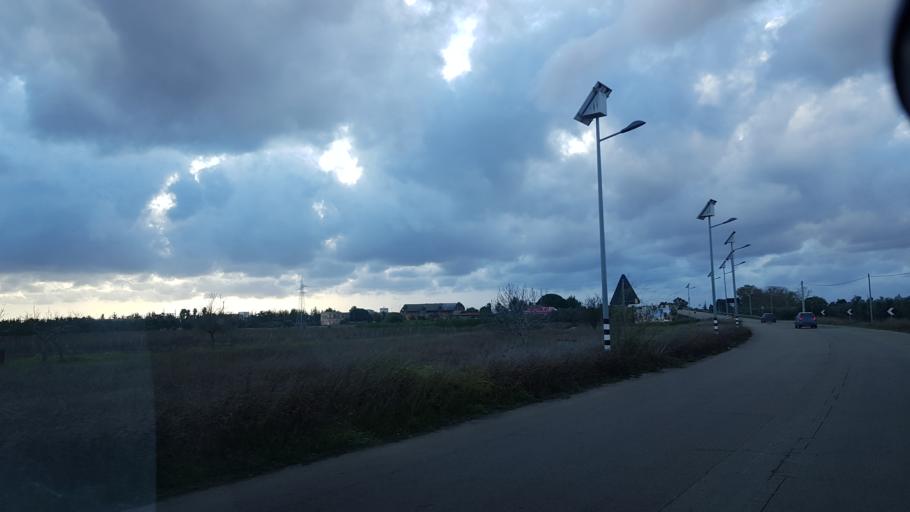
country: IT
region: Apulia
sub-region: Provincia di Brindisi
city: San Pietro Vernotico
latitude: 40.4998
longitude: 18.0023
